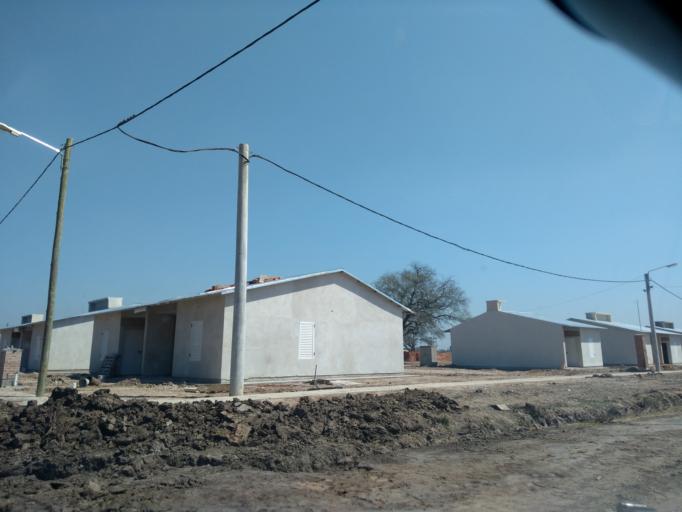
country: AR
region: Chaco
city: Resistencia
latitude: -27.4134
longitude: -58.9559
